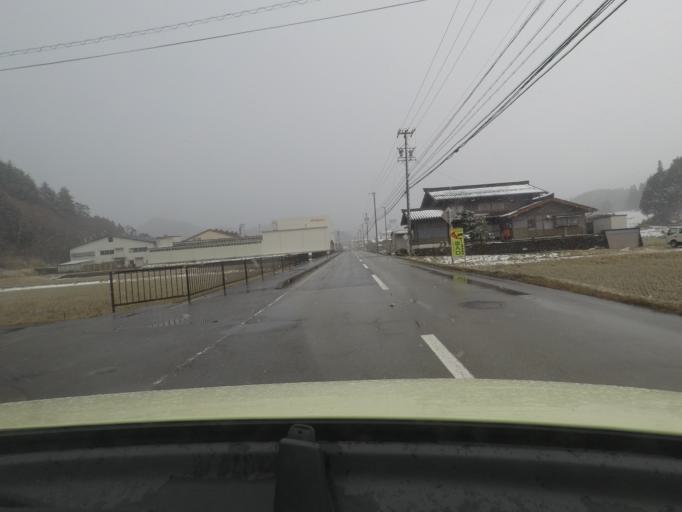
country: JP
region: Gifu
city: Takayama
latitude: 36.1466
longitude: 137.2901
